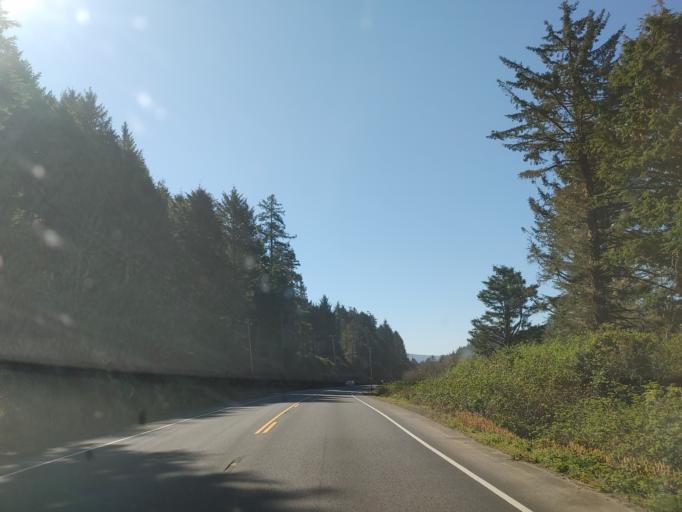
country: US
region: Oregon
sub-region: Tillamook County
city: Rockaway Beach
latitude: 45.5824
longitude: -123.9460
